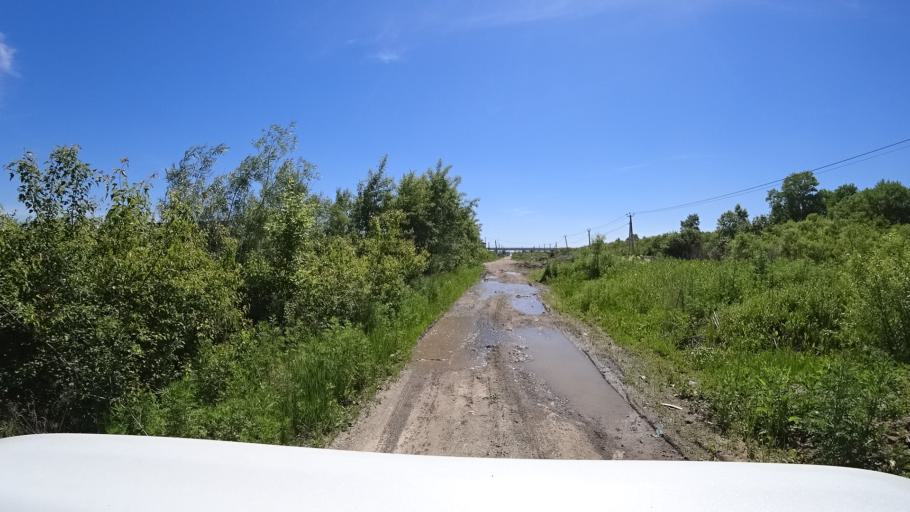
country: RU
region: Khabarovsk Krai
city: Topolevo
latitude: 48.4853
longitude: 135.1761
